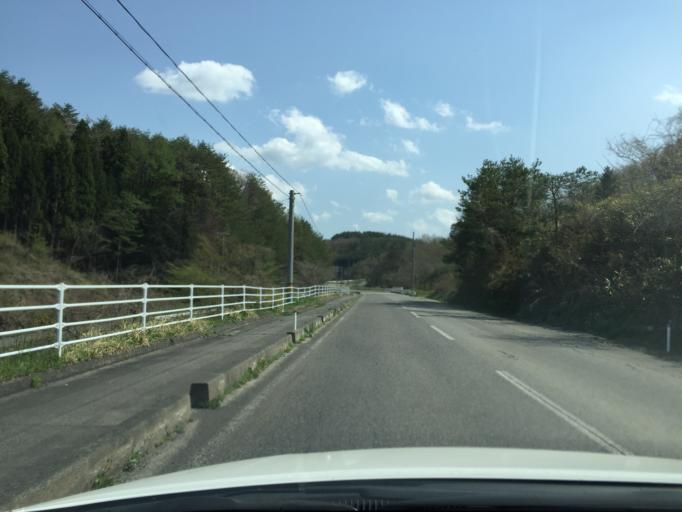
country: JP
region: Fukushima
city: Namie
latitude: 37.4028
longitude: 140.7996
